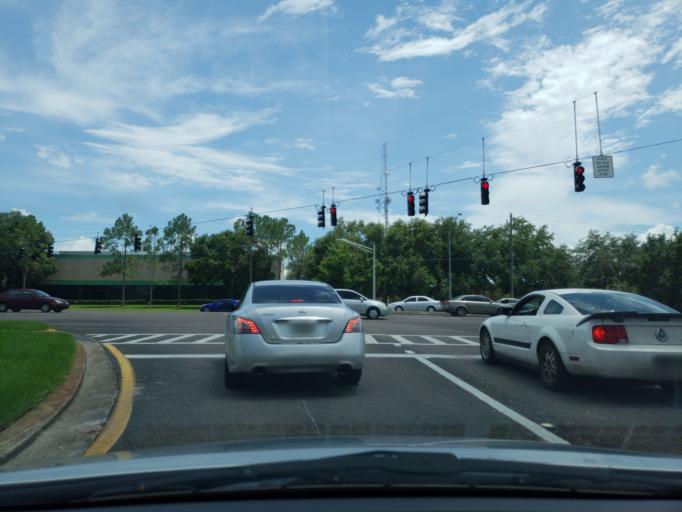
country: US
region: Florida
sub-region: Hillsborough County
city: University
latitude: 28.0549
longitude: -82.4133
